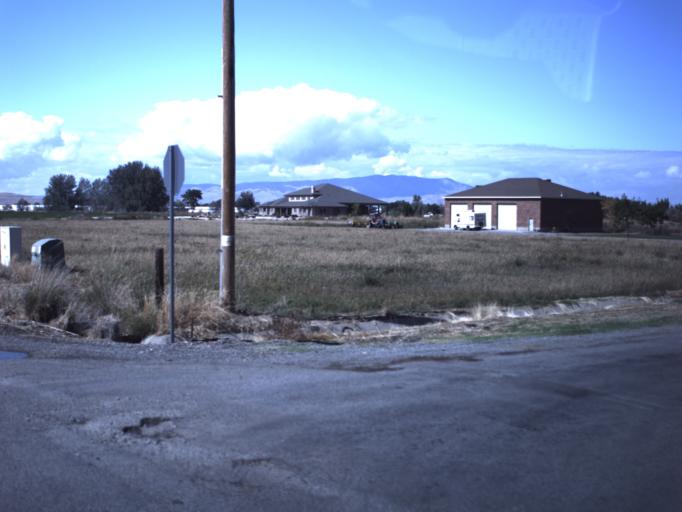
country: US
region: Utah
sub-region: Utah County
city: Benjamin
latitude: 40.1148
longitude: -111.7114
